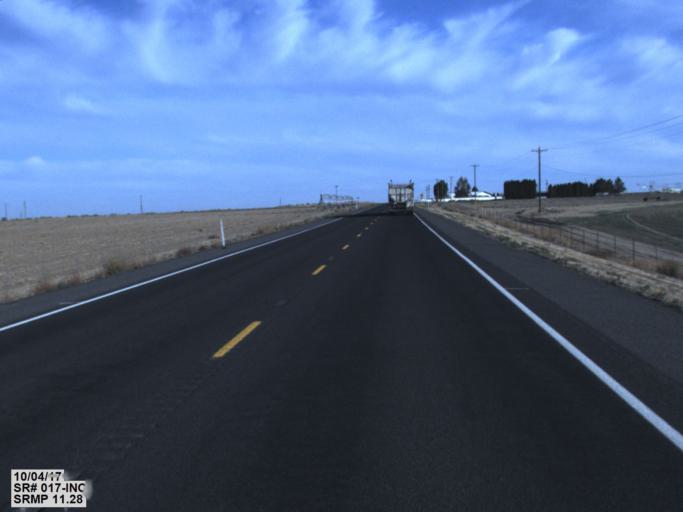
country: US
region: Washington
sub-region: Franklin County
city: Basin City
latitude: 46.6157
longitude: -119.0062
